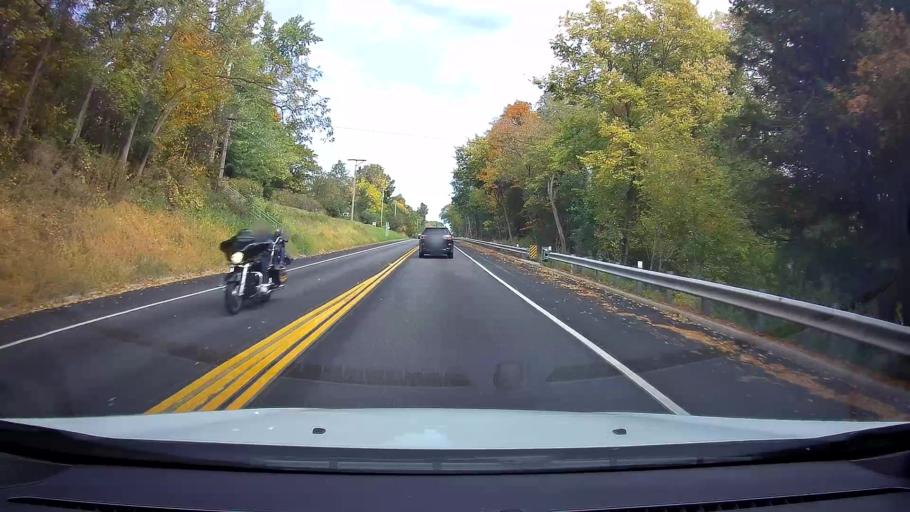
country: US
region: Minnesota
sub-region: Washington County
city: Scandia
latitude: 45.2006
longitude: -92.7704
